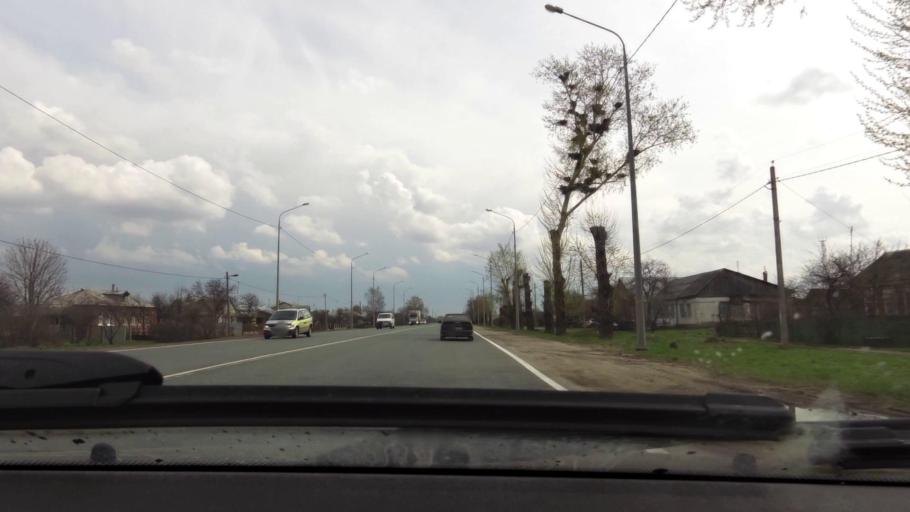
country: RU
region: Rjazan
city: Bagramovo
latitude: 54.7511
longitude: 39.4235
